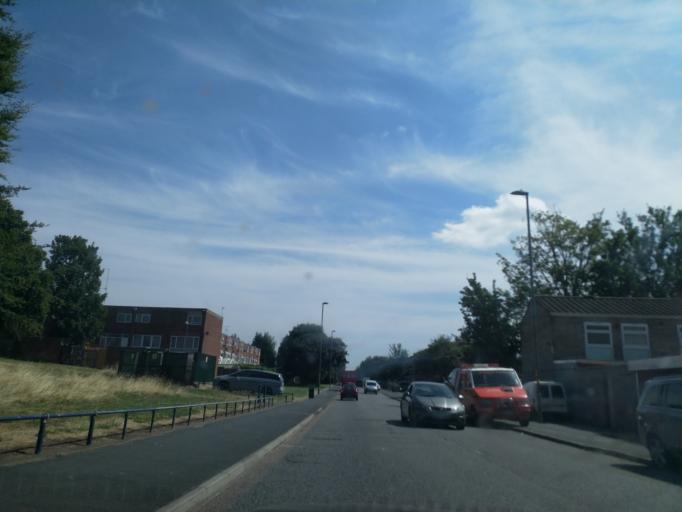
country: GB
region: England
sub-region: City and Borough of Birmingham
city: Birmingham
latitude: 52.4992
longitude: -1.8910
